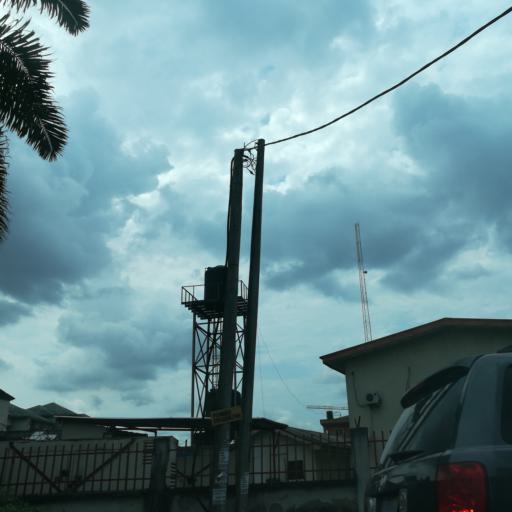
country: NG
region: Rivers
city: Port Harcourt
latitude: 4.8244
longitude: 7.0010
